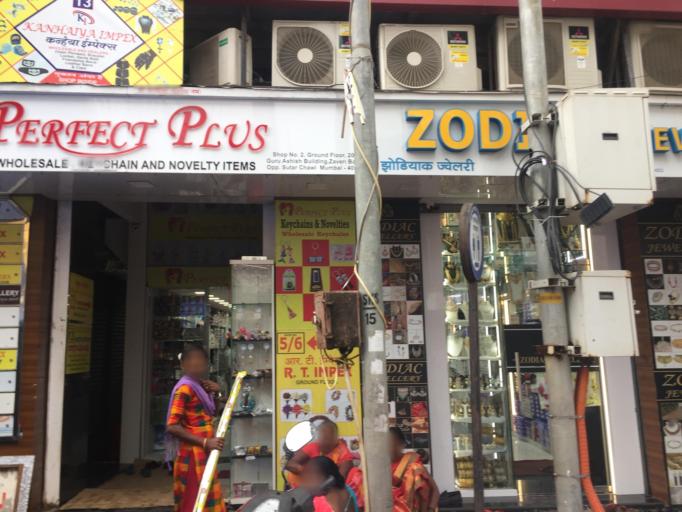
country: IN
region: Maharashtra
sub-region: Raigarh
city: Uran
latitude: 18.9494
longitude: 72.8319
